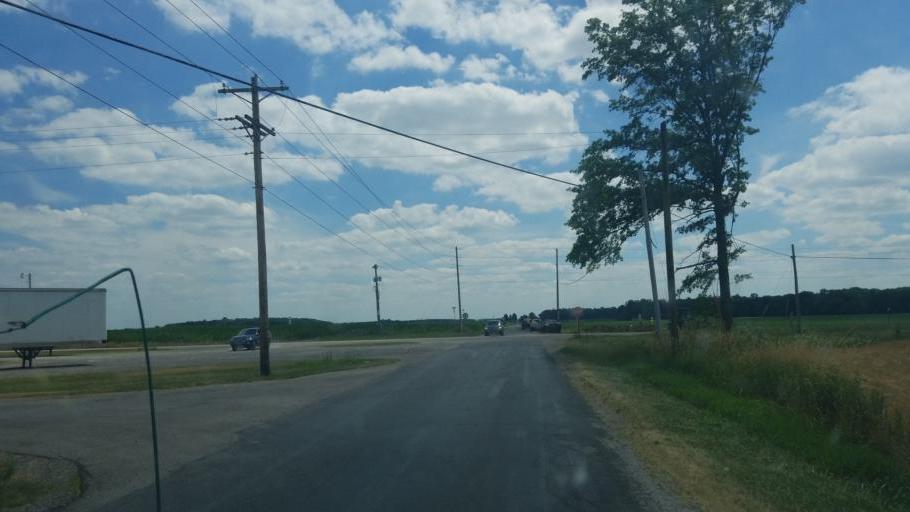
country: US
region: Ohio
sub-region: Williams County
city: Edgerton
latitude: 41.4488
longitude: -84.6911
